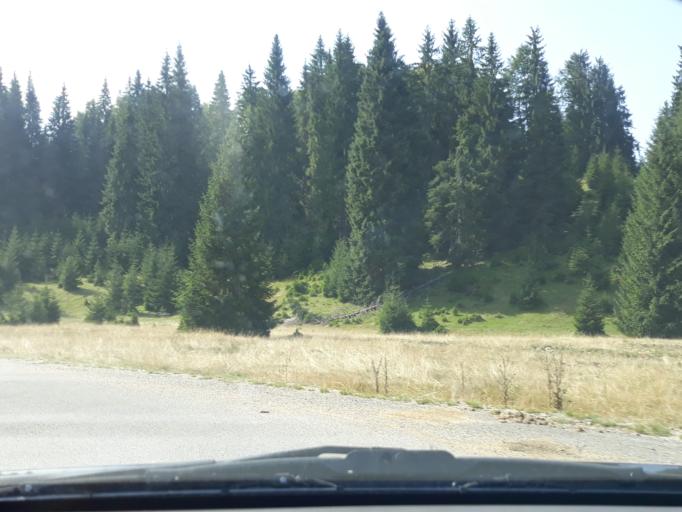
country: RO
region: Alba
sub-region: Comuna Arieseni
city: Arieseni
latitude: 46.6010
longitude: 22.7087
